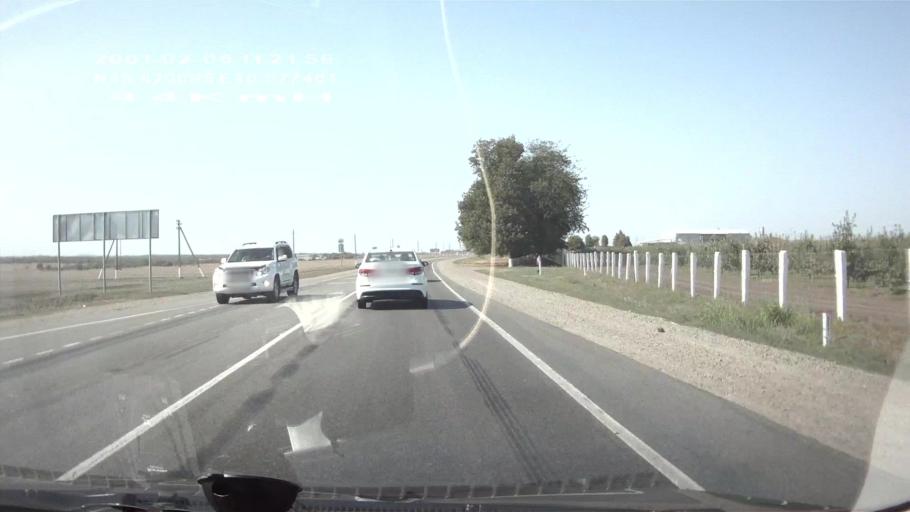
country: RU
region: Krasnodarskiy
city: Kropotkin
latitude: 45.4700
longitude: 40.5768
